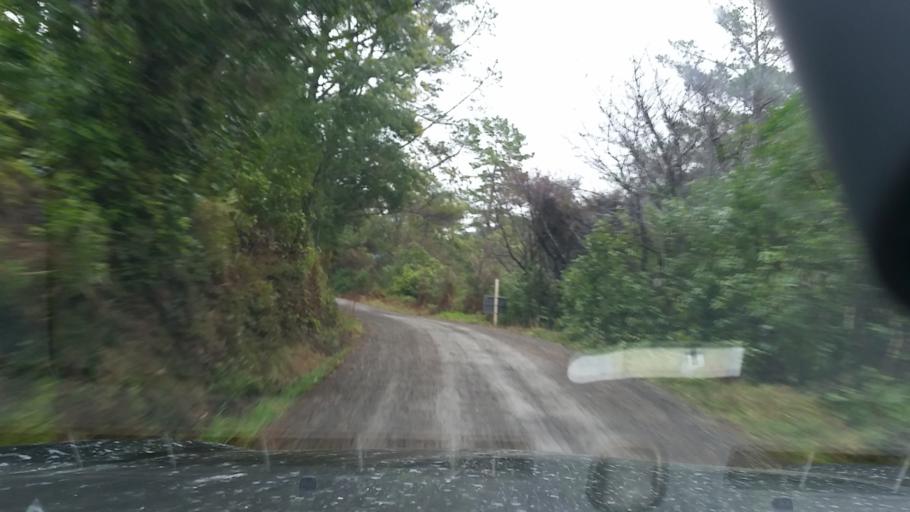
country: NZ
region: Nelson
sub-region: Nelson City
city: Nelson
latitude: -41.3557
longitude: 173.6285
